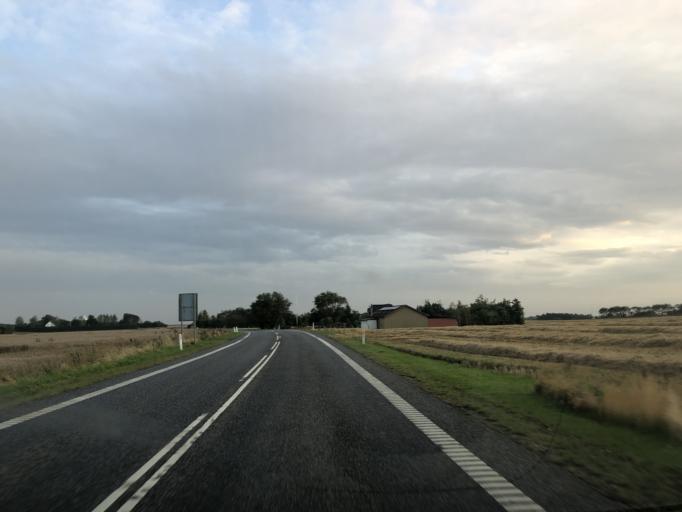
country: DK
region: Central Jutland
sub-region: Holstebro Kommune
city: Vinderup
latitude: 56.6080
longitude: 8.8782
